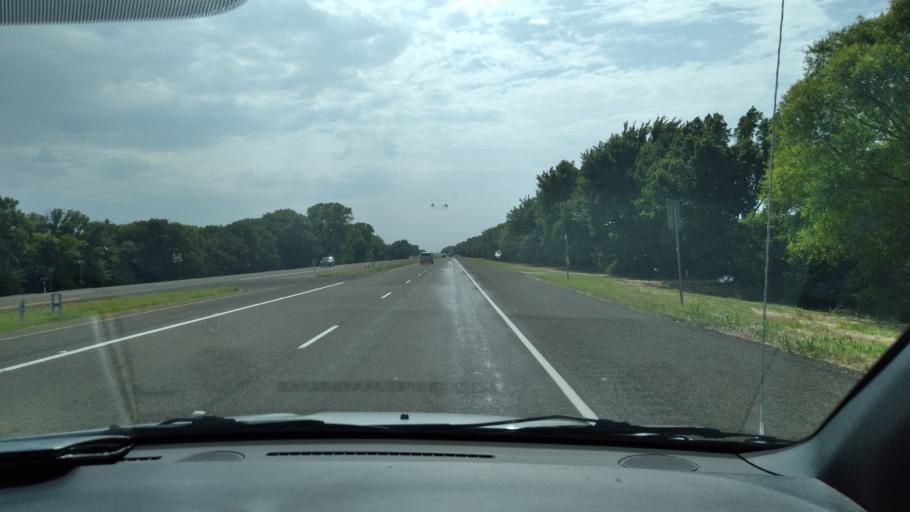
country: US
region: Texas
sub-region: Navarro County
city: Kerens
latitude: 32.1256
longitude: -96.2750
